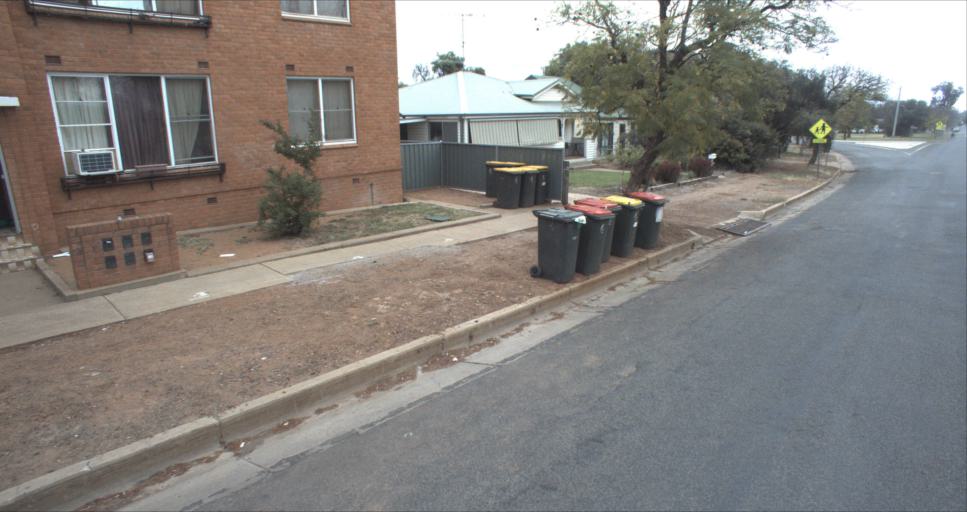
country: AU
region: New South Wales
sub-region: Leeton
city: Leeton
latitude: -34.5501
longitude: 146.4050
